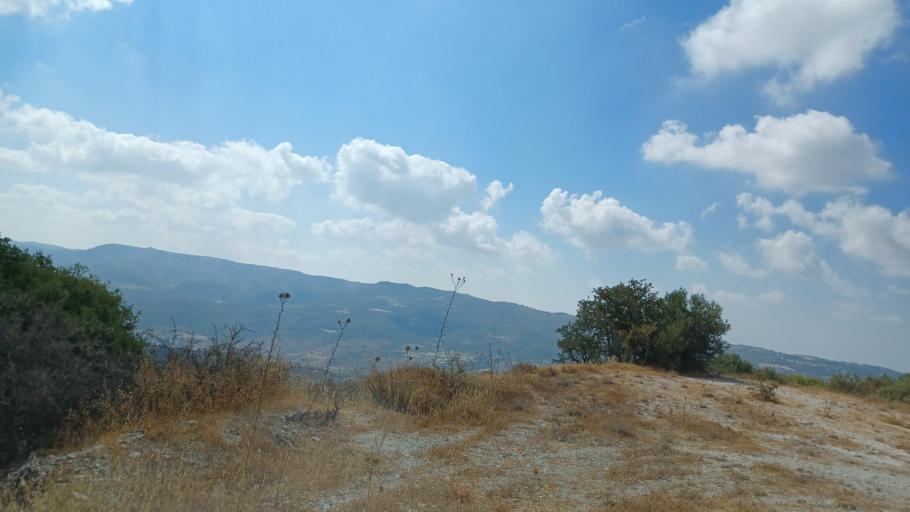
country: CY
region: Limassol
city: Pachna
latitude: 34.7997
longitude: 32.6656
